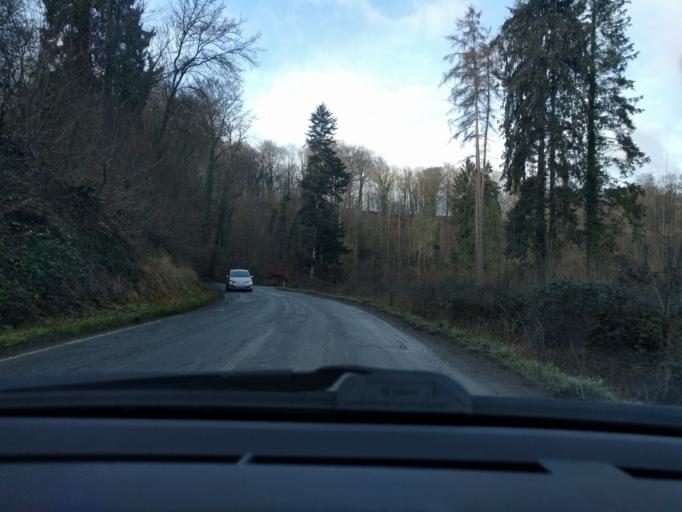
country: BE
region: Wallonia
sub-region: Province de Namur
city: Noville-les-Bois
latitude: 50.4947
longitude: 4.9516
